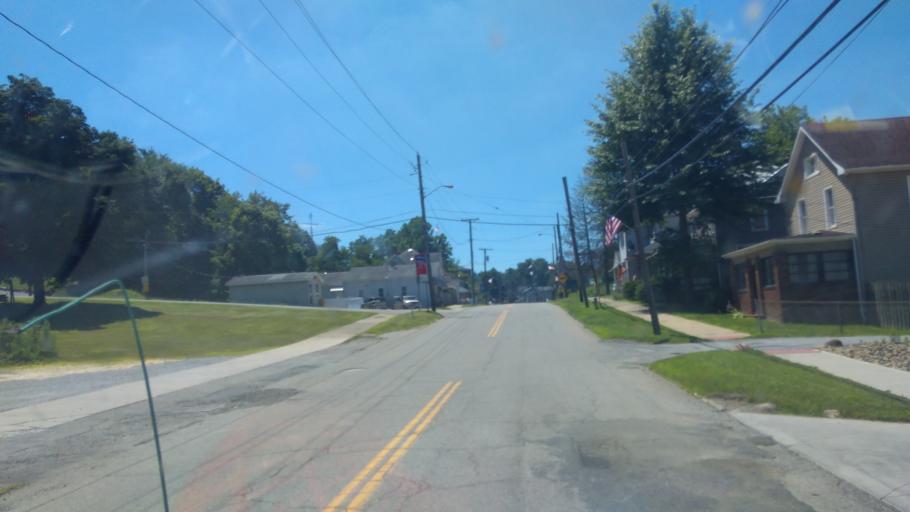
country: US
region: Ohio
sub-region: Columbiana County
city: Salineville
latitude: 40.6234
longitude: -80.8355
